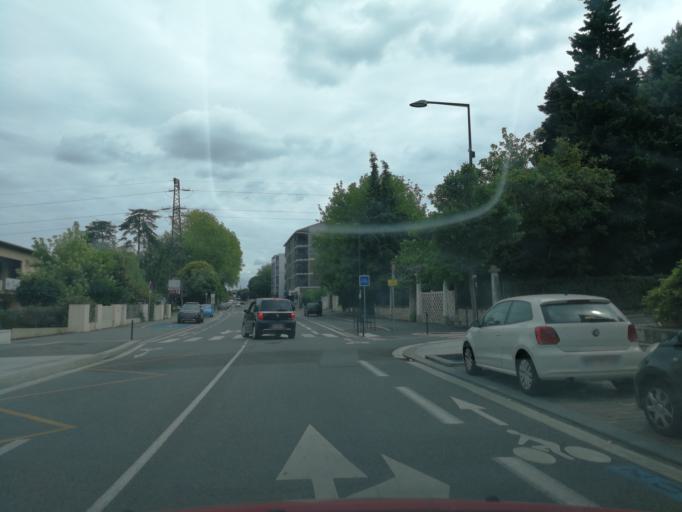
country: FR
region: Midi-Pyrenees
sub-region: Departement de la Haute-Garonne
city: Ramonville-Saint-Agne
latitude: 43.5508
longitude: 1.4702
